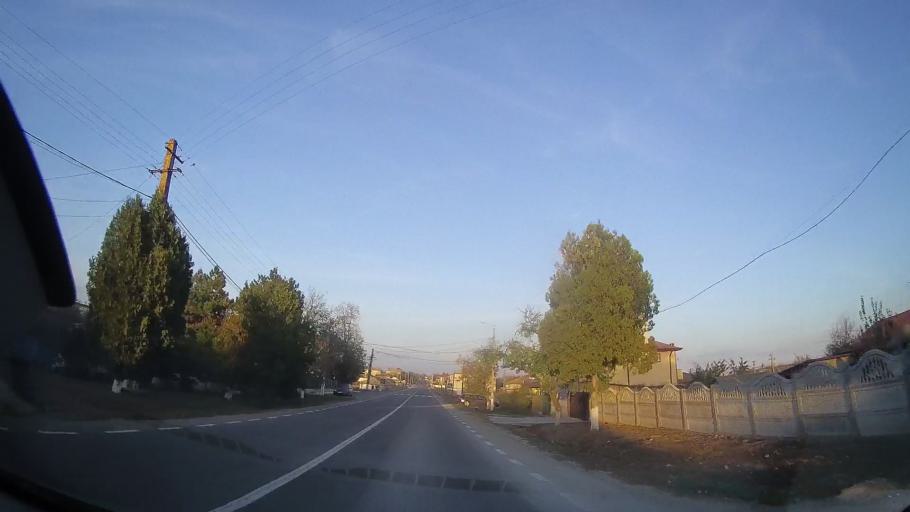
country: RO
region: Constanta
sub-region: Comuna Amzacea
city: Amzacea
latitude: 43.9579
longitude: 28.3911
